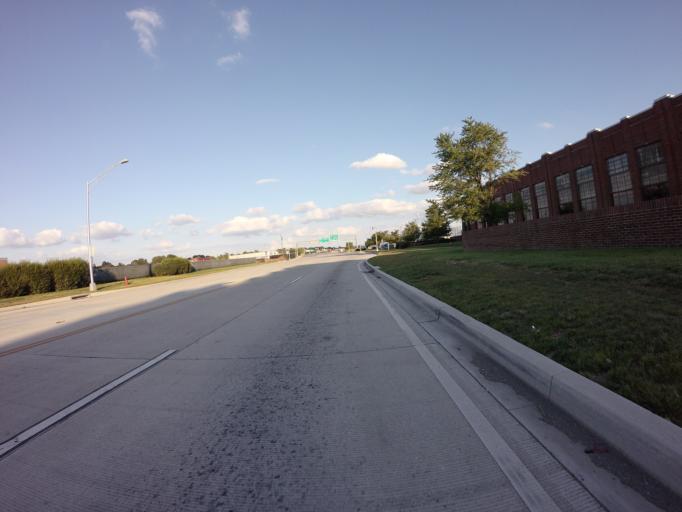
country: US
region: Maryland
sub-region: Baltimore County
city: Dundalk
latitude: 39.2594
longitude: -76.5388
